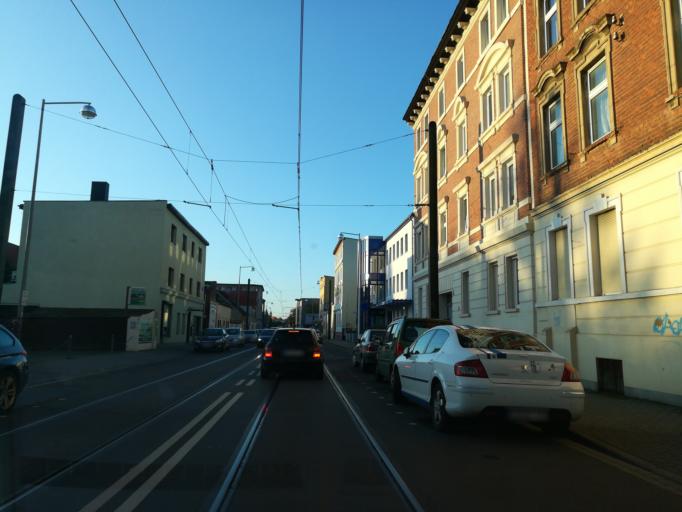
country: DE
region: Saxony-Anhalt
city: Magdeburg
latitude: 52.1180
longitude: 11.6631
